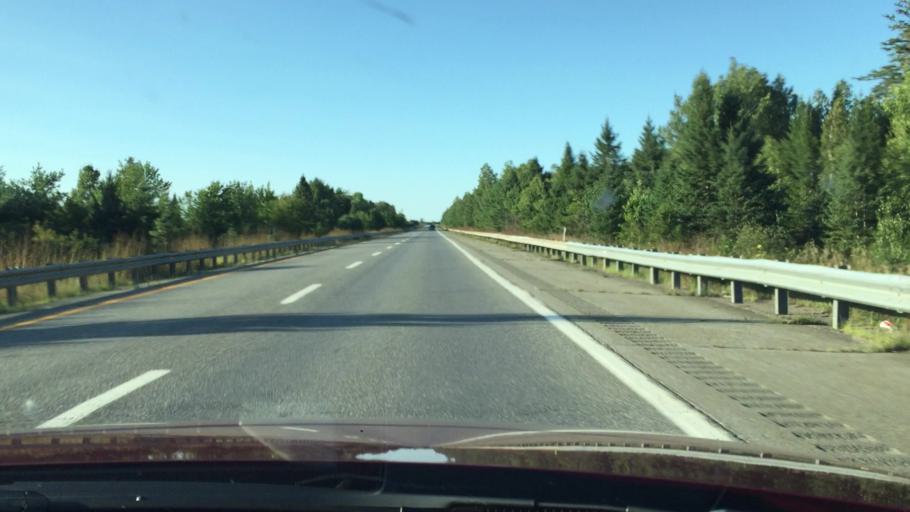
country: US
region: Maine
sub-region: Penobscot County
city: Medway
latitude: 45.6490
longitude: -68.4984
